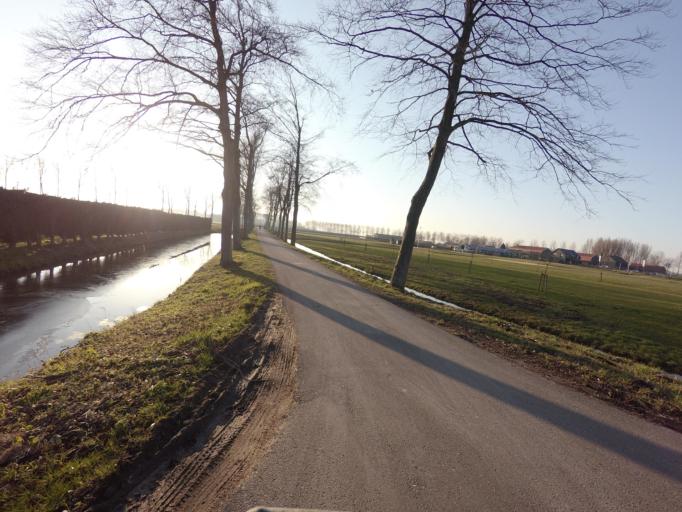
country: NL
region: South Holland
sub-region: Gemeente Giessenlanden
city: Giessenburg
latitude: 51.8969
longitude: 4.9305
